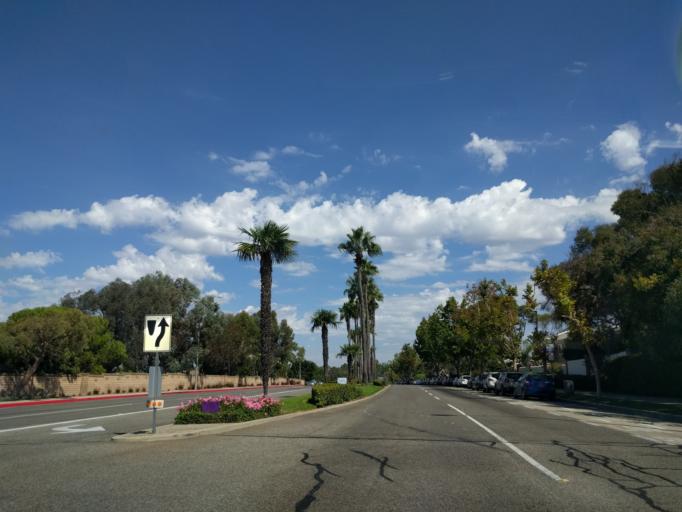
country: US
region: California
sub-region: Orange County
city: Dana Point
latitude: 33.4809
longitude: -117.6977
